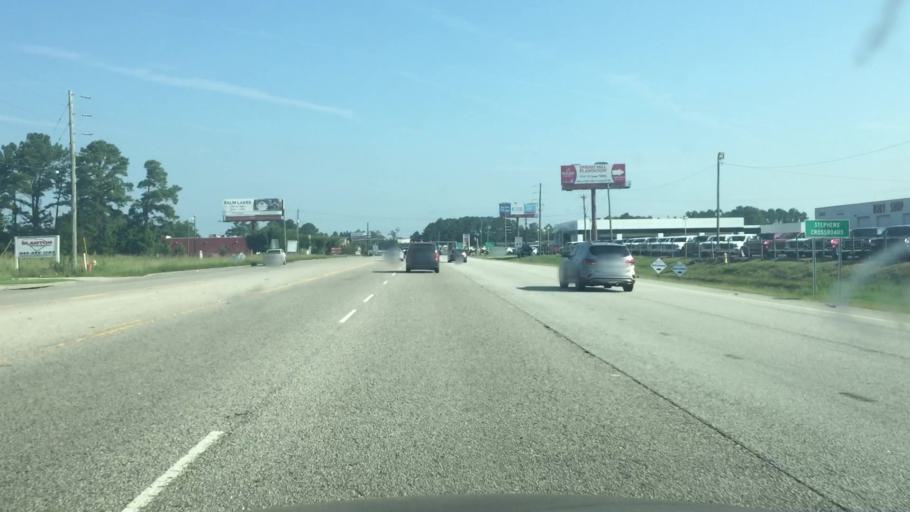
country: US
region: South Carolina
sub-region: Horry County
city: North Myrtle Beach
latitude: 33.8815
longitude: -78.6867
